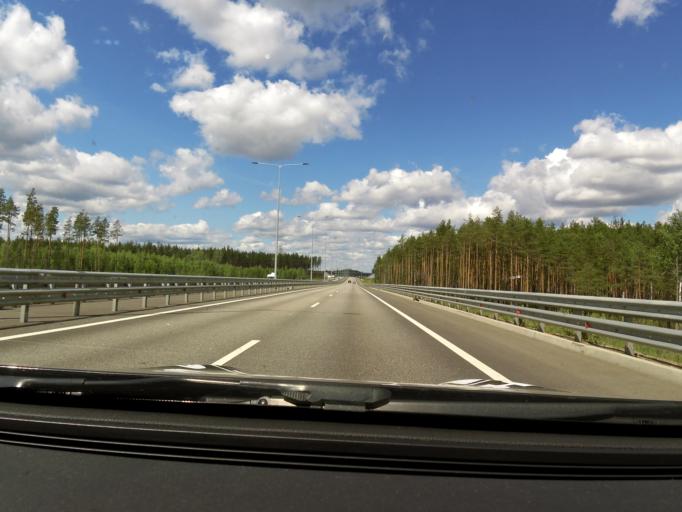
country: RU
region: Tverskaya
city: Krasnomayskiy
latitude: 57.4682
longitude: 34.3614
